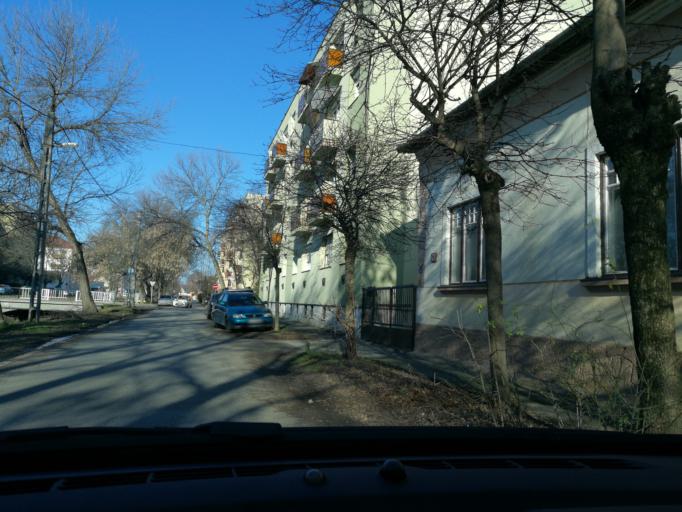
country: HU
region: Szabolcs-Szatmar-Bereg
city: Nyiregyhaza
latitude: 47.9460
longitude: 21.7114
